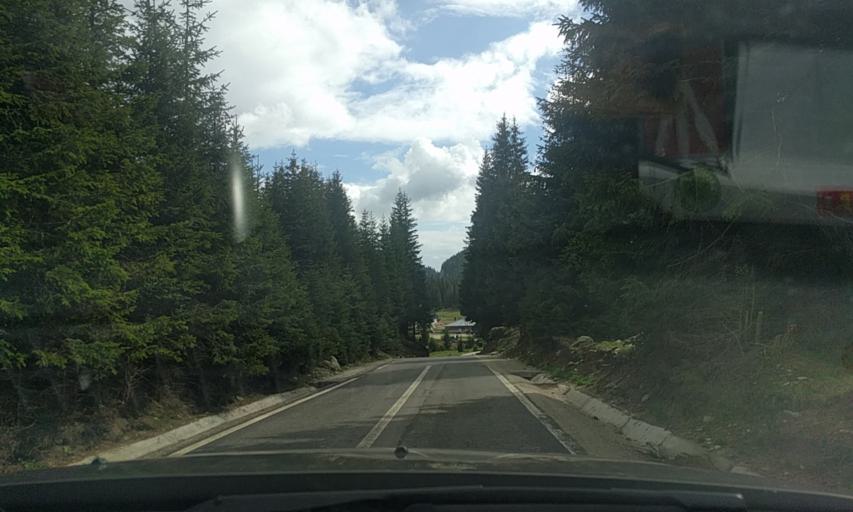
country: RO
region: Prahova
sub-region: Oras Busteni
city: Busteni
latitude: 45.3803
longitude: 25.4382
